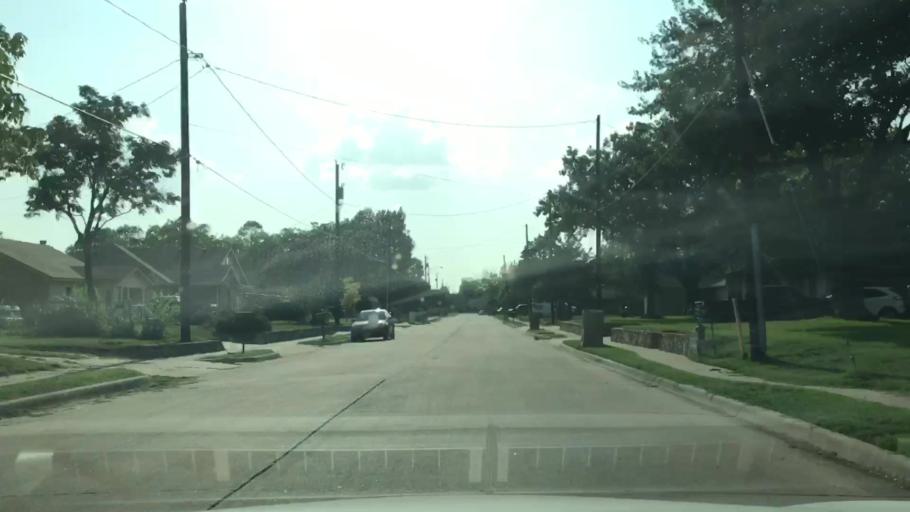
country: US
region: Texas
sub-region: Dallas County
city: Irving
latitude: 32.8199
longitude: -96.9384
